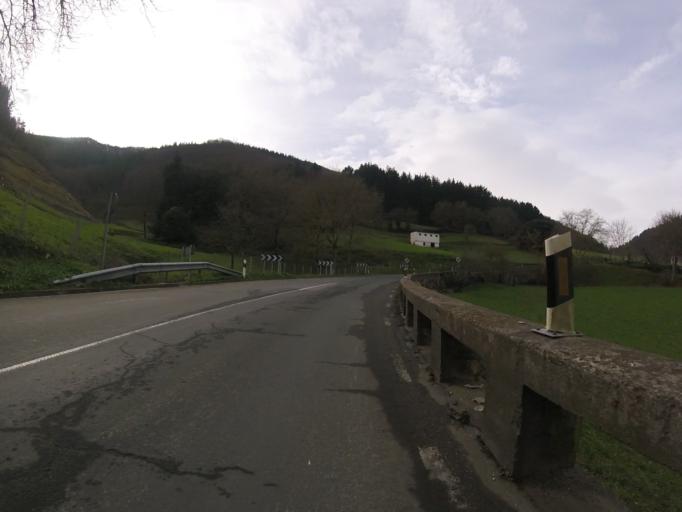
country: ES
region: Basque Country
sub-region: Provincia de Guipuzcoa
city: Albiztur
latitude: 43.1238
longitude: -2.1389
